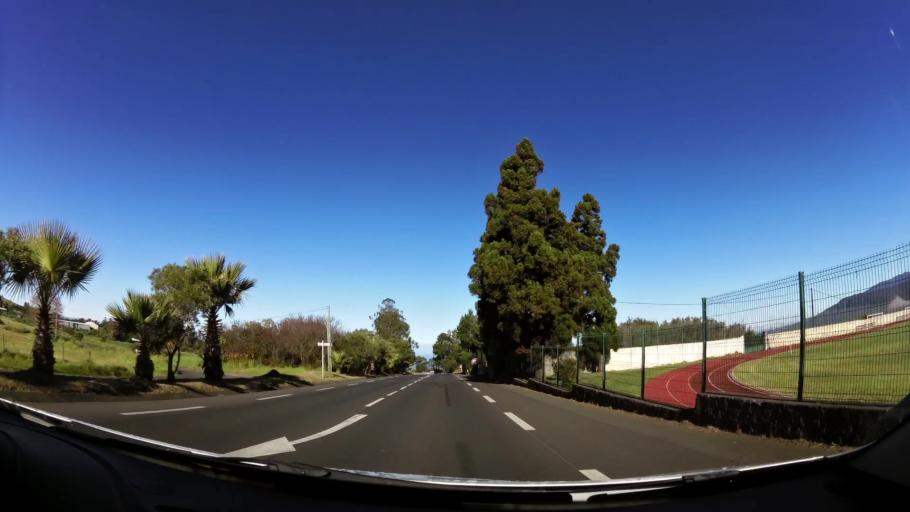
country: RE
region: Reunion
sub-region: Reunion
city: Le Tampon
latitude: -21.2063
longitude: 55.5687
